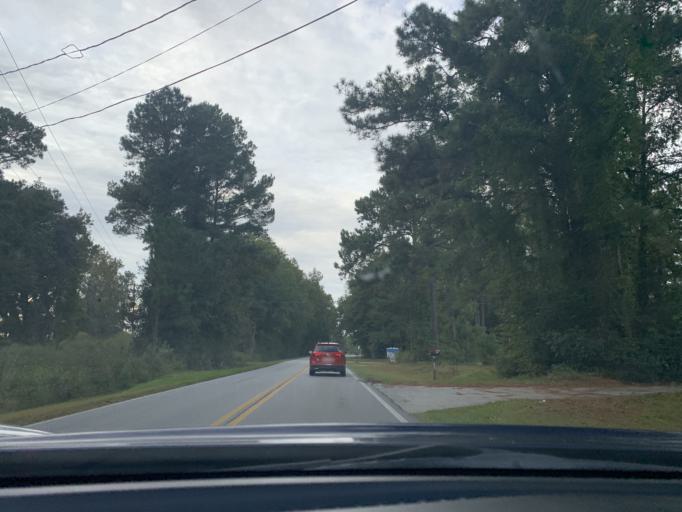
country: US
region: Georgia
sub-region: Chatham County
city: Georgetown
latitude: 32.0368
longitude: -81.2577
